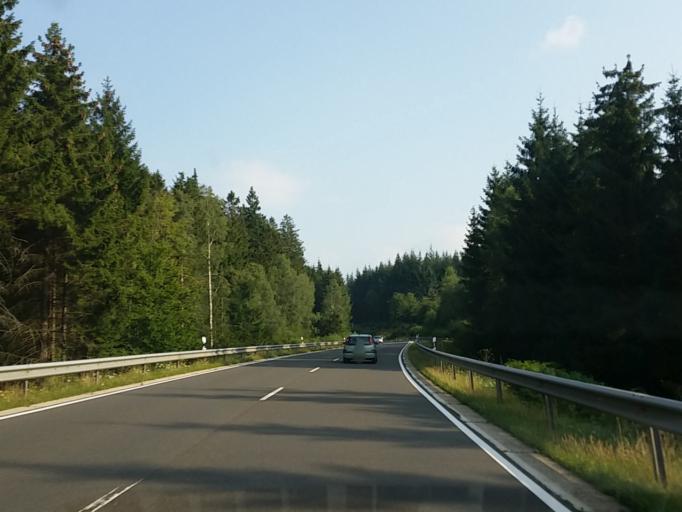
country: DE
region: Rheinland-Pfalz
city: Lorscheid
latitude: 49.7002
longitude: 6.8522
